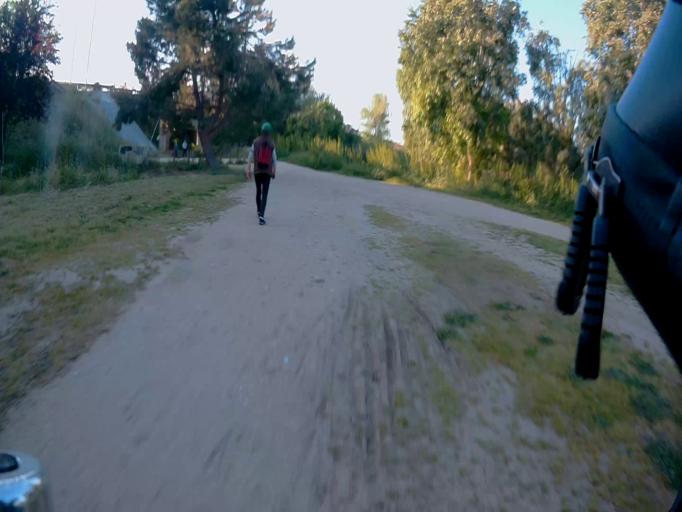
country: ES
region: Madrid
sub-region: Provincia de Madrid
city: Fuenlabrada
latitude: 40.3155
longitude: -3.7938
